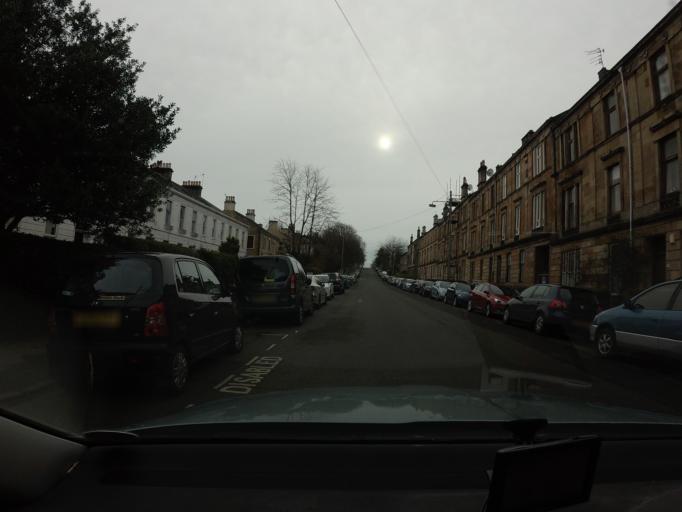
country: GB
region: Scotland
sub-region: Glasgow City
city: Glasgow
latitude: 55.8333
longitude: -4.2635
